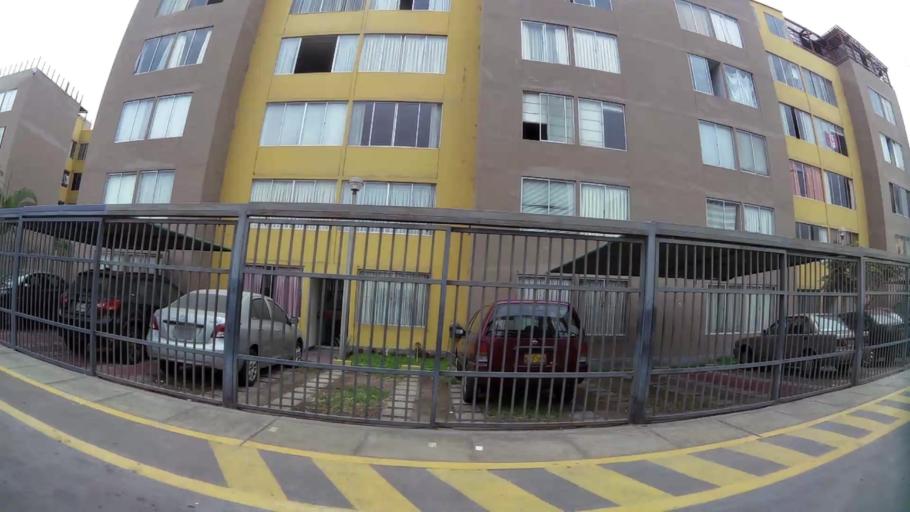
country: PE
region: Lima
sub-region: Lima
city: Surco
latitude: -12.1437
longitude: -77.0069
